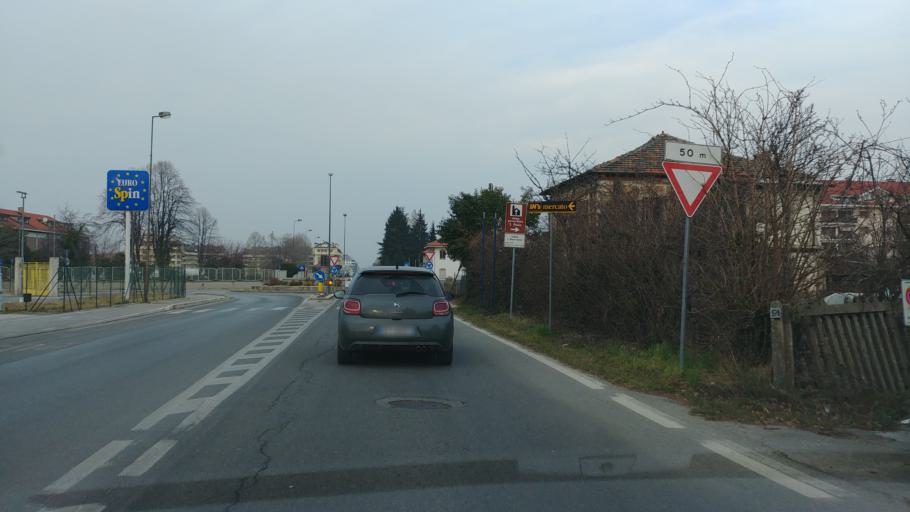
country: IT
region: Piedmont
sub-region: Provincia di Cuneo
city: Cuneo
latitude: 44.3713
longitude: 7.5291
